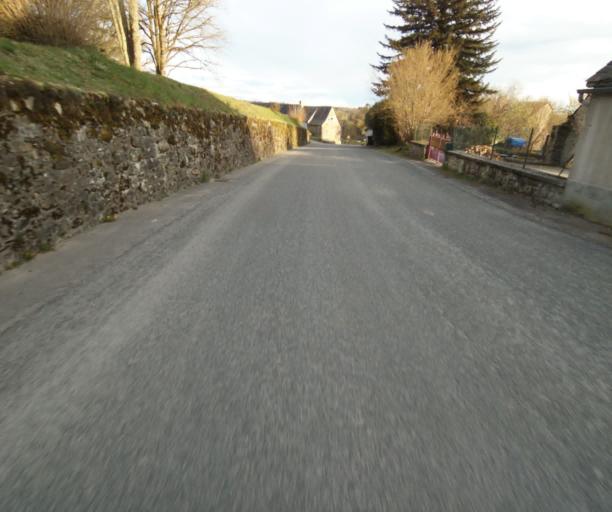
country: FR
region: Limousin
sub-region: Departement de la Correze
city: Argentat
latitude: 45.2218
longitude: 1.9788
